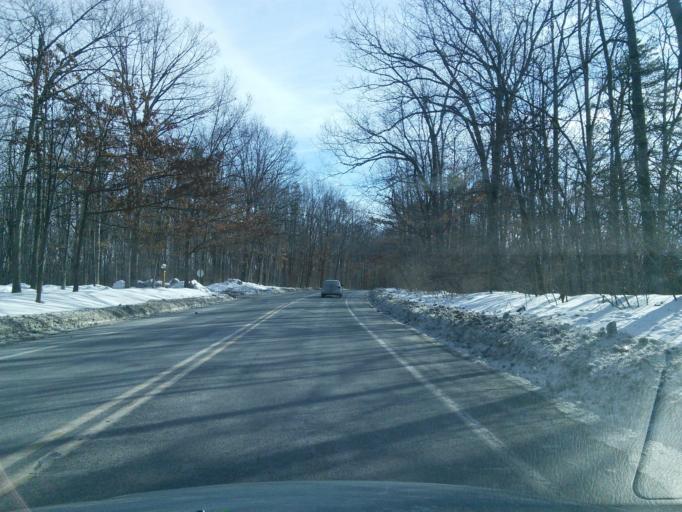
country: US
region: Pennsylvania
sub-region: Centre County
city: Park Forest Village
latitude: 40.8236
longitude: -77.8890
